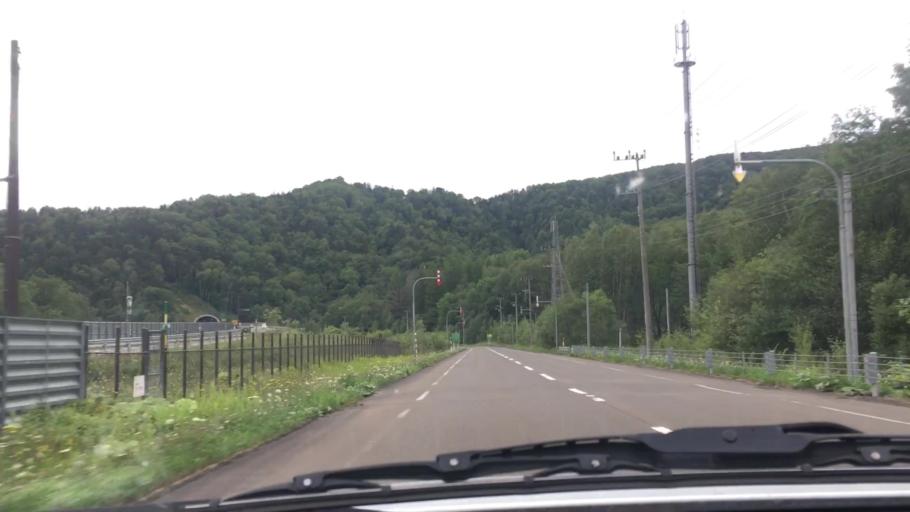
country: JP
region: Hokkaido
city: Shimo-furano
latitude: 43.0655
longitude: 142.5380
